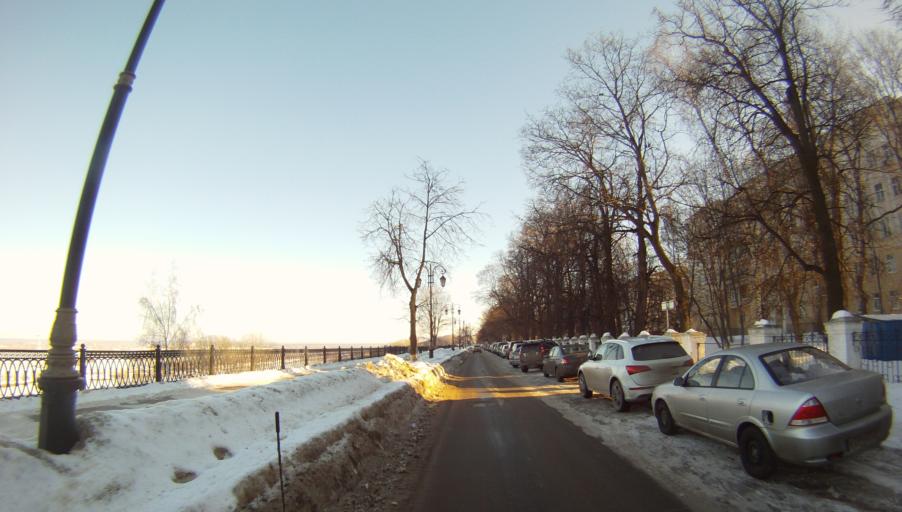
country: RU
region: Nizjnij Novgorod
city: Nizhniy Novgorod
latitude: 56.3267
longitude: 44.0277
